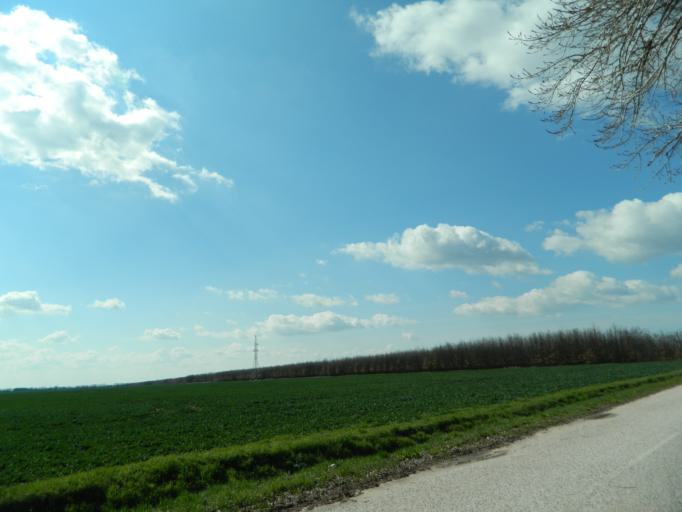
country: HU
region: Fejer
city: Szabadbattyan
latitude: 47.1226
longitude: 18.4117
